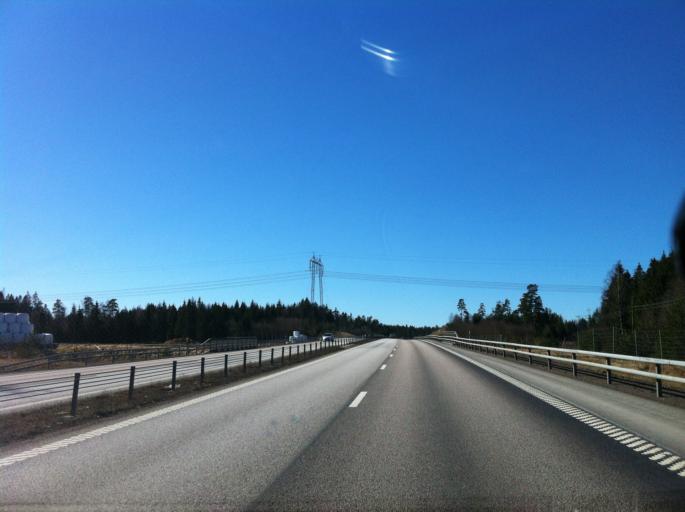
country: SE
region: Vaestra Goetaland
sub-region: Vanersborgs Kommun
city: Vanersborg
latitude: 58.3766
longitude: 12.3393
